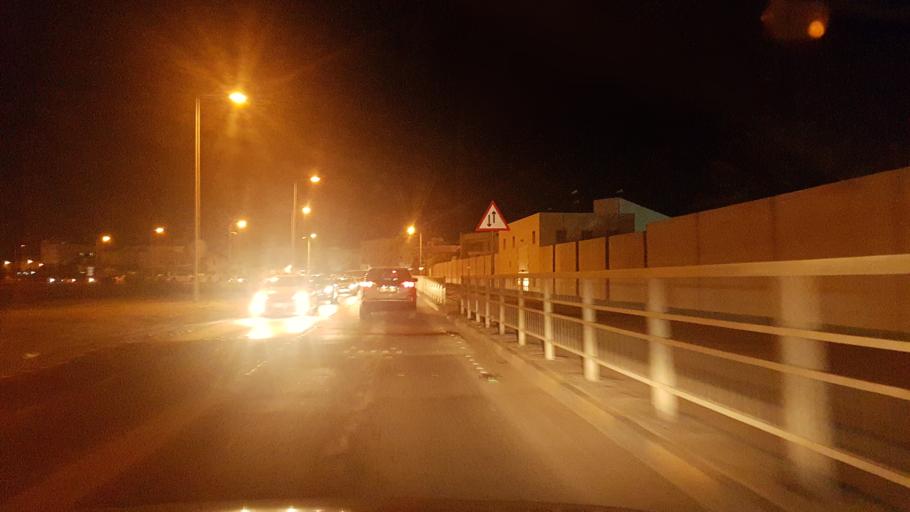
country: BH
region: Muharraq
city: Al Muharraq
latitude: 26.2810
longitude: 50.6280
